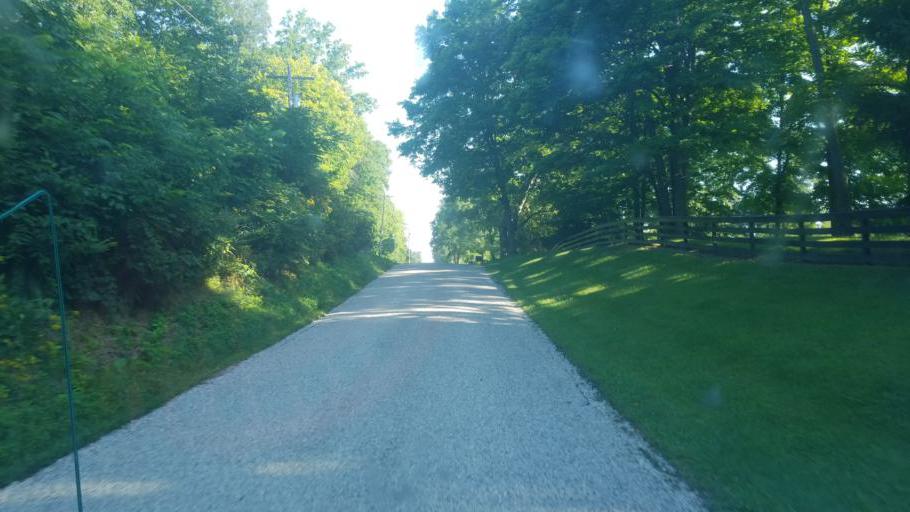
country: US
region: Ohio
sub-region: Ashland County
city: Ashland
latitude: 40.9428
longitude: -82.3397
